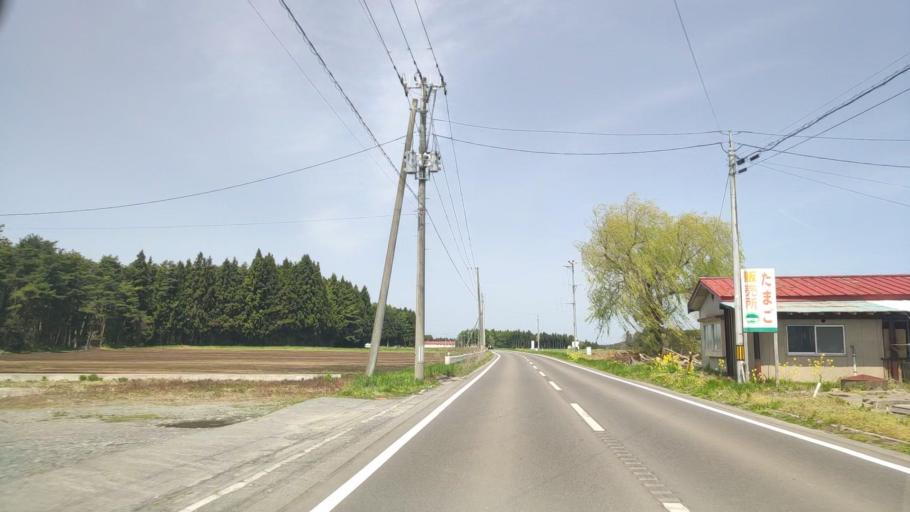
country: JP
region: Aomori
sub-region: Hachinohe Shi
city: Uchimaru
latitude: 40.5380
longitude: 141.4014
